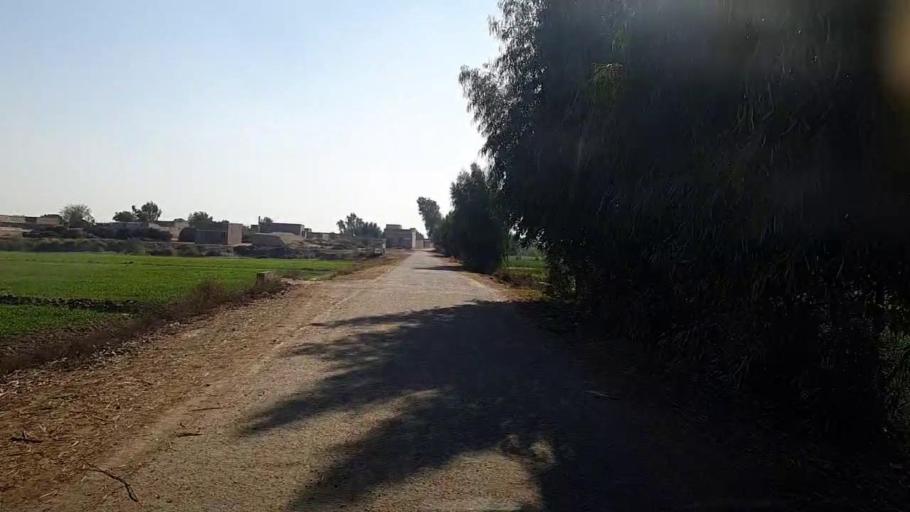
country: PK
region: Sindh
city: Khairpur
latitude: 27.9617
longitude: 69.7295
